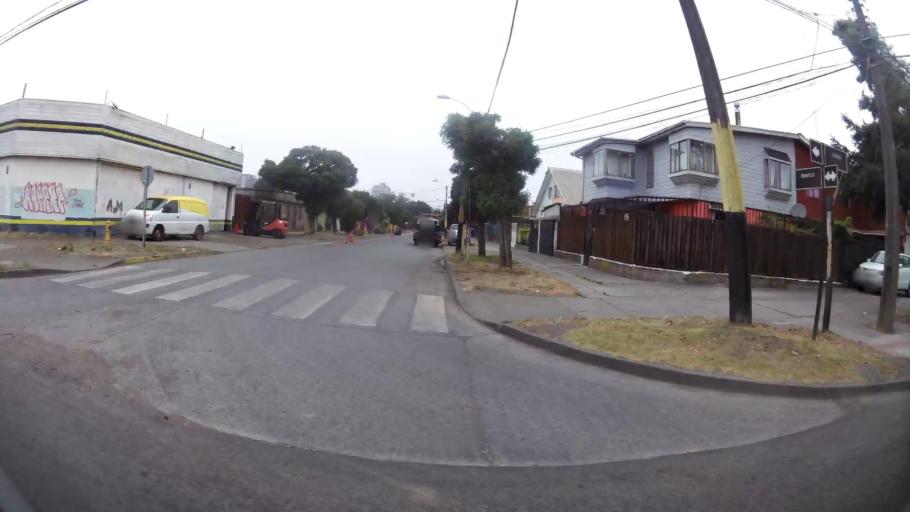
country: CL
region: Biobio
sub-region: Provincia de Concepcion
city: Concepcion
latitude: -36.8108
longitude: -73.0534
